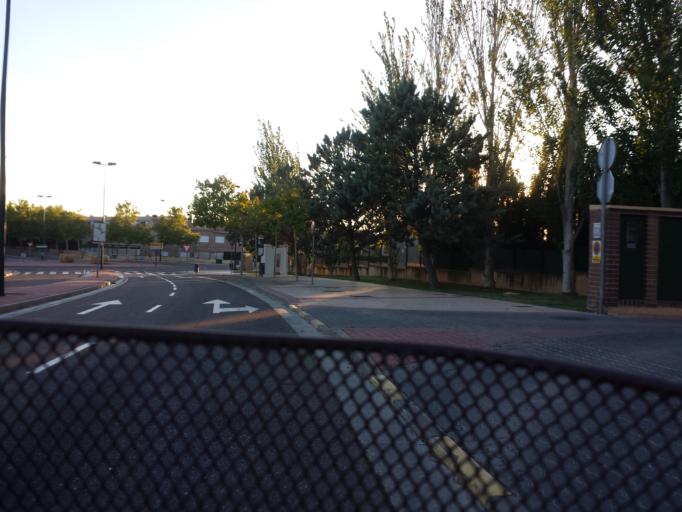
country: ES
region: Aragon
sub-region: Provincia de Zaragoza
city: Montecanal
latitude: 41.6315
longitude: -0.9390
